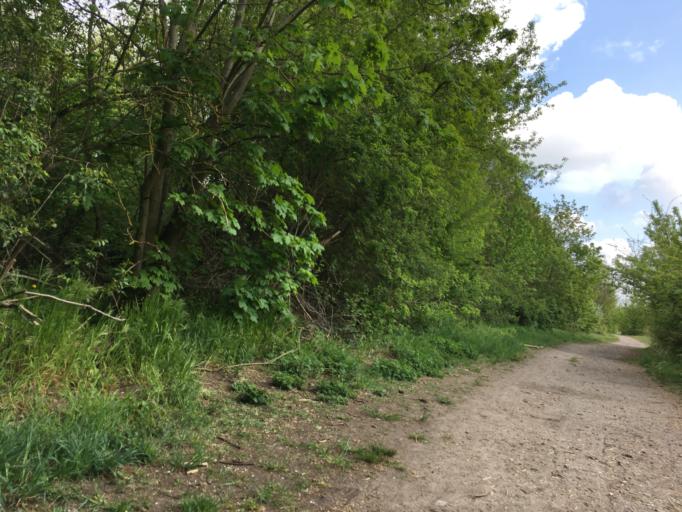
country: DE
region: Berlin
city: Blankenfelde
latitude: 52.6293
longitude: 13.4136
